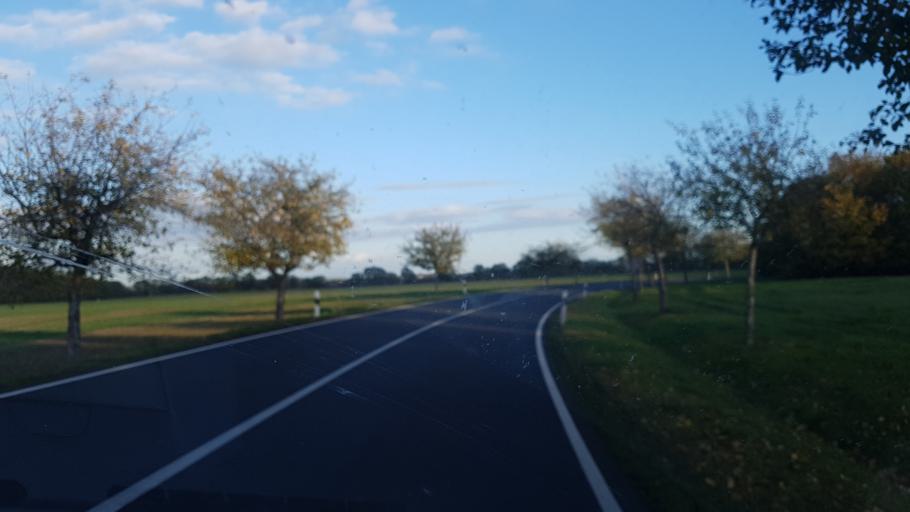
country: DE
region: Saxony
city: Oschatz
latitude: 51.3288
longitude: 13.0524
